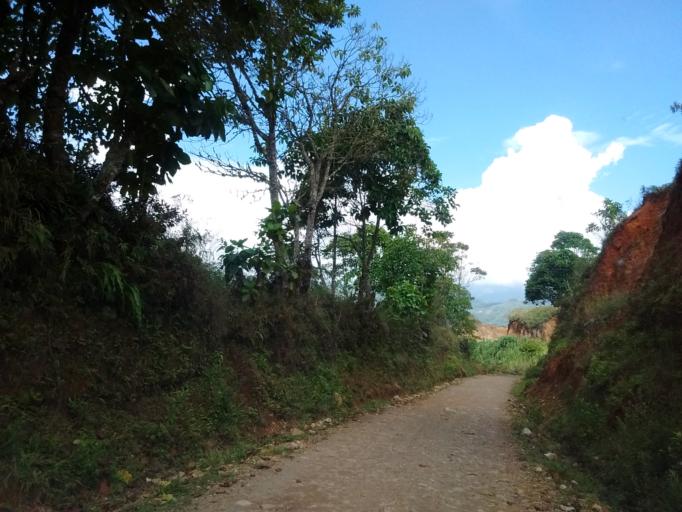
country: CO
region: Cauca
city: Morales
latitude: 2.6873
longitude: -76.7413
